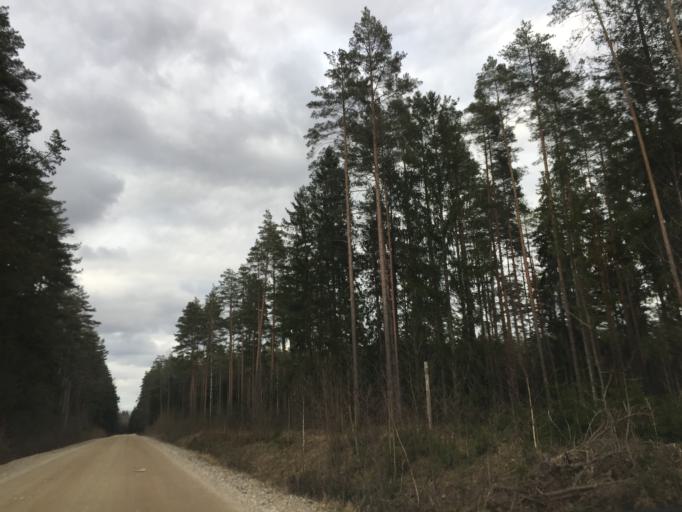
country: LV
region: Jaunjelgava
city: Jaunjelgava
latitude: 56.5903
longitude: 25.0414
